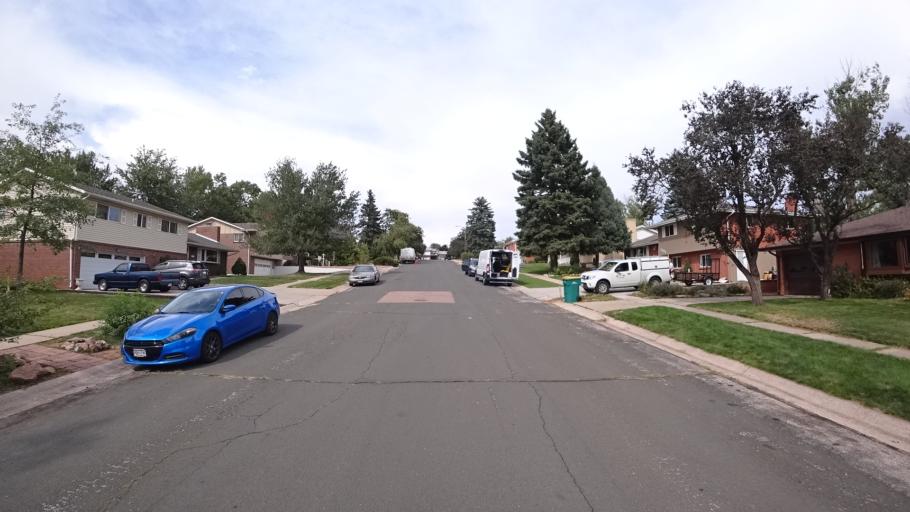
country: US
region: Colorado
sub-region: El Paso County
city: Colorado Springs
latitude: 38.8633
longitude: -104.7793
